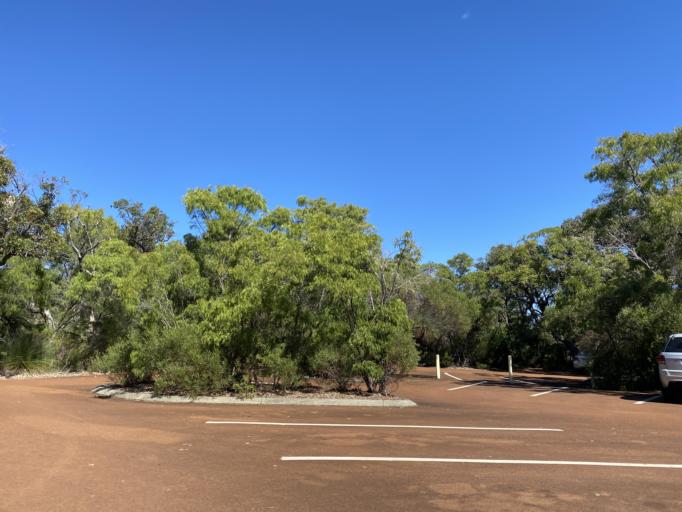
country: AU
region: Western Australia
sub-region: Augusta-Margaret River Shire
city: Margaret River
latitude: -34.0793
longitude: 115.0291
